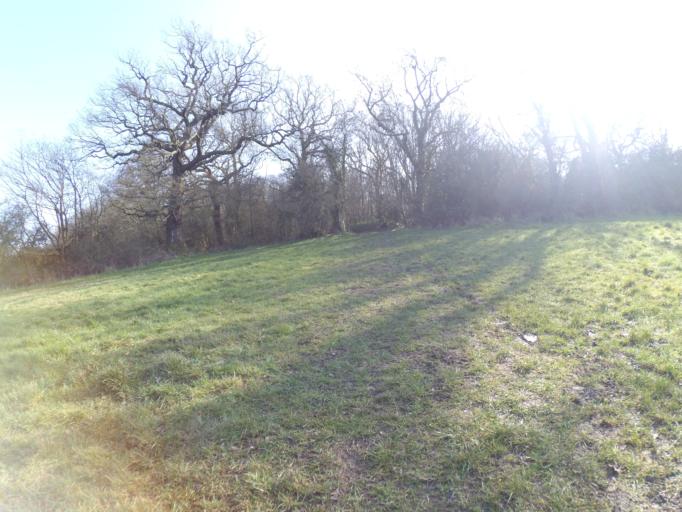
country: GB
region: England
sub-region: Greater London
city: Wembley
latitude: 51.5752
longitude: -0.2830
